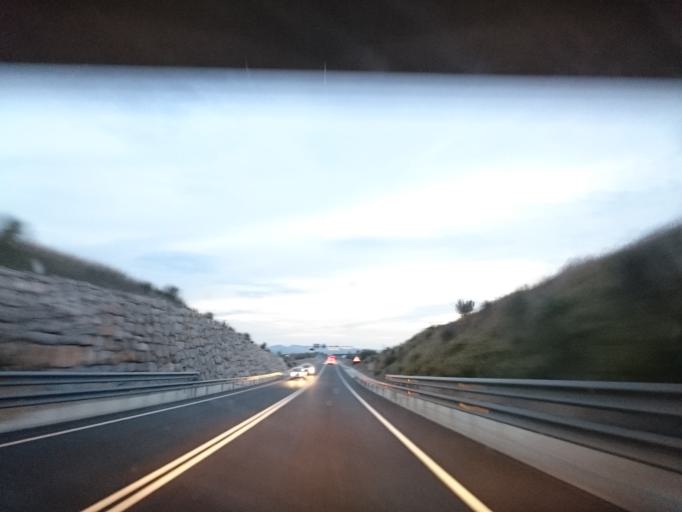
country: ES
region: Catalonia
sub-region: Provincia de Barcelona
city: La Granada
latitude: 41.3762
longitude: 1.7121
